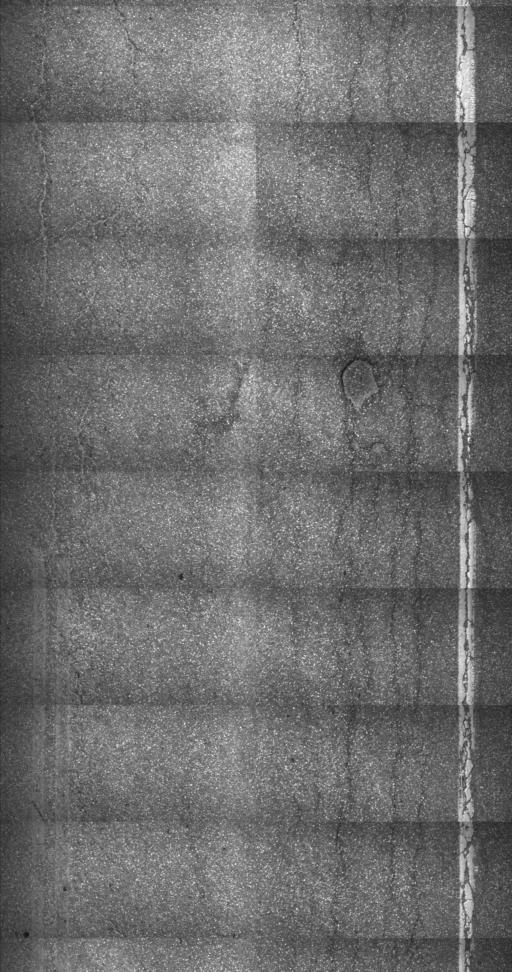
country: US
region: Vermont
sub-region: Franklin County
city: Saint Albans
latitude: 44.8119
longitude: -73.1267
